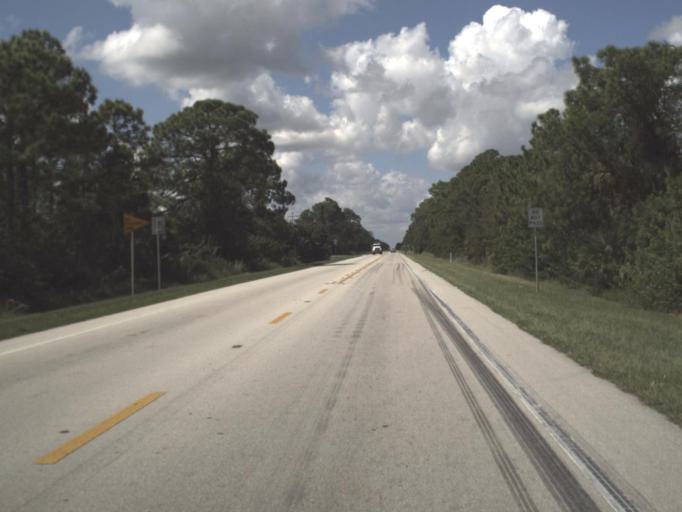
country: US
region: Florida
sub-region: Collier County
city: Immokalee
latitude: 26.5061
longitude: -81.5153
